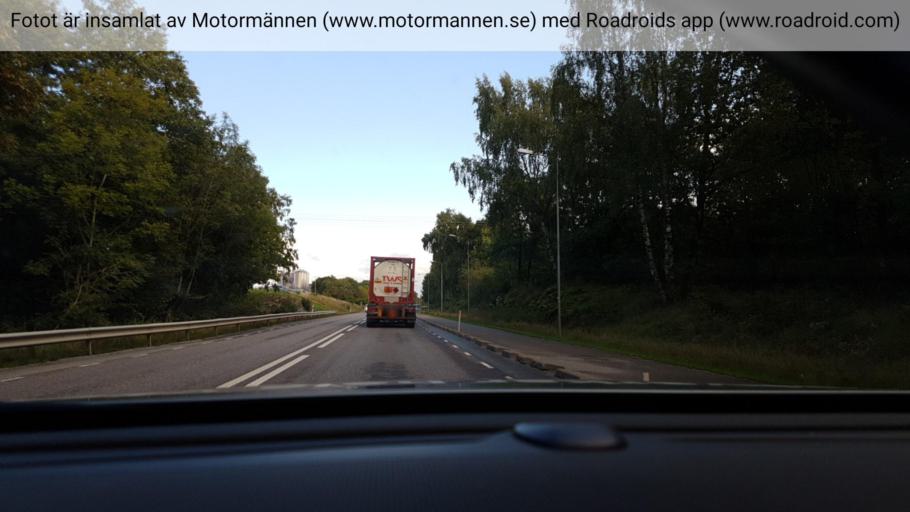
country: SE
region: Vaestra Goetaland
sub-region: Stenungsunds Kommun
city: Stenungsund
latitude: 58.0769
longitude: 11.8352
